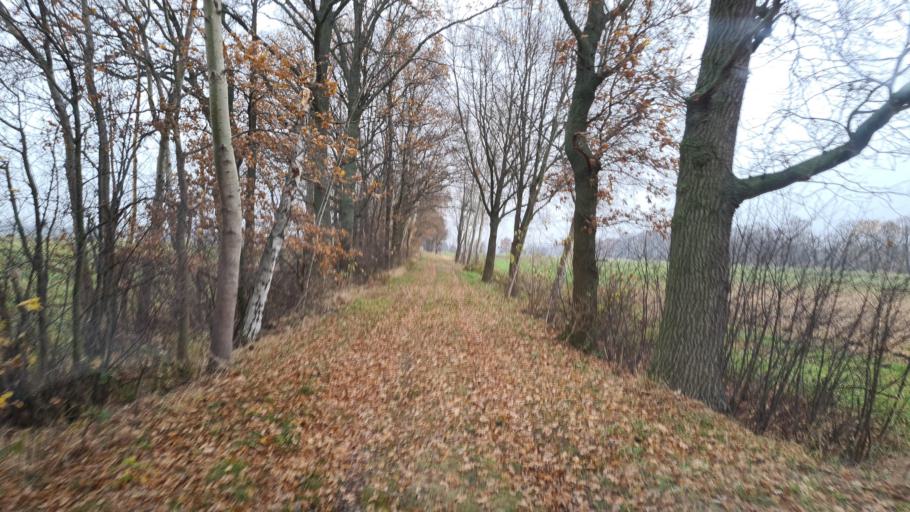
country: DE
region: Brandenburg
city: Schraden
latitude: 51.4130
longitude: 13.7110
